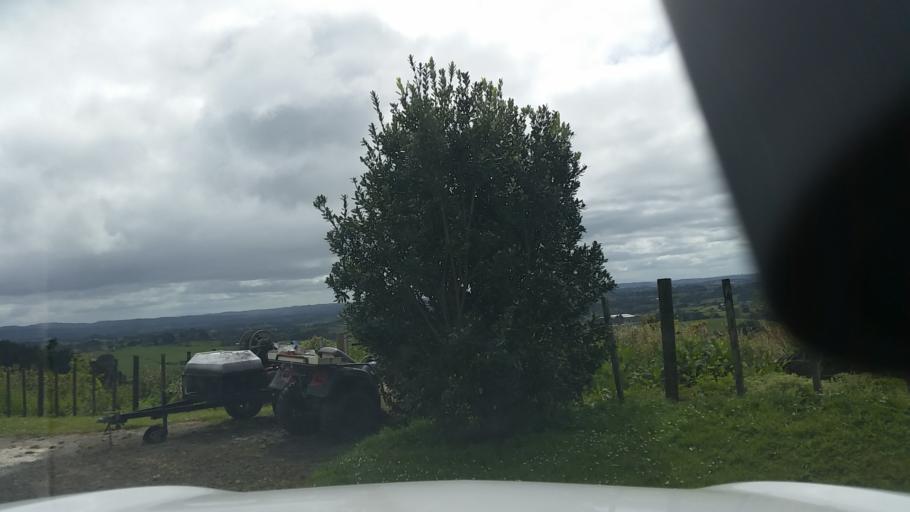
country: NZ
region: Auckland
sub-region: Auckland
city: Muriwai Beach
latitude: -36.8407
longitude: 174.5116
